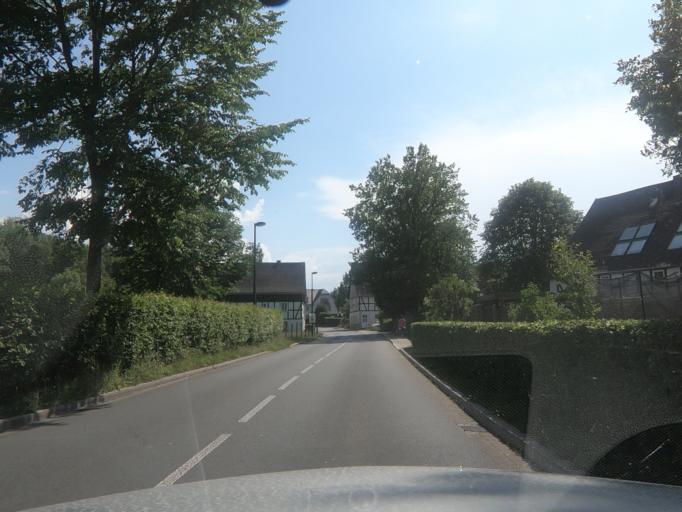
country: DE
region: North Rhine-Westphalia
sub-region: Regierungsbezirk Arnsberg
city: Finnentrop
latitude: 51.1235
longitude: 7.9751
